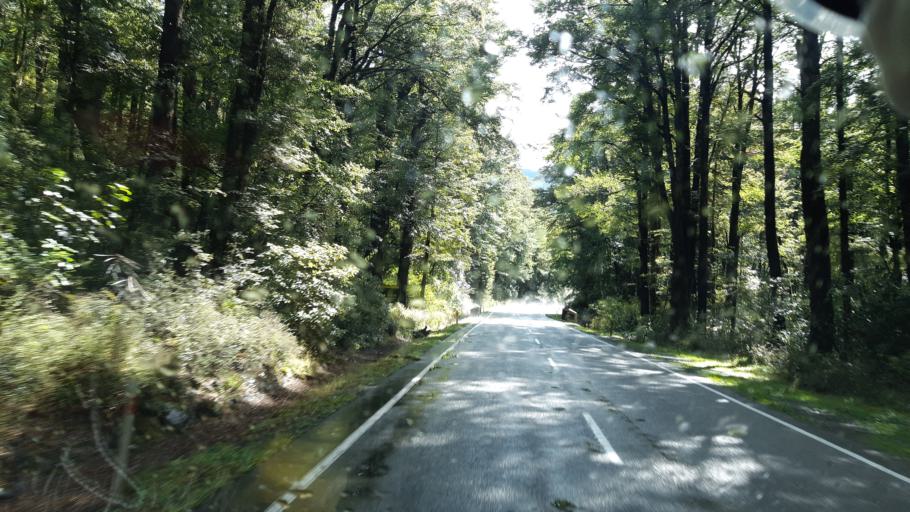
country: NZ
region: Canterbury
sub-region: Hurunui District
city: Amberley
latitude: -42.3795
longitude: 172.2799
